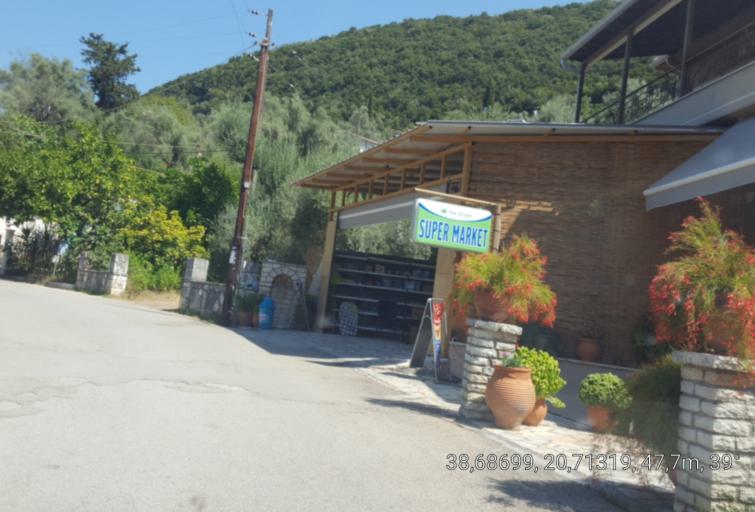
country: GR
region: Ionian Islands
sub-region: Lefkada
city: Nidri
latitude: 38.6869
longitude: 20.7132
